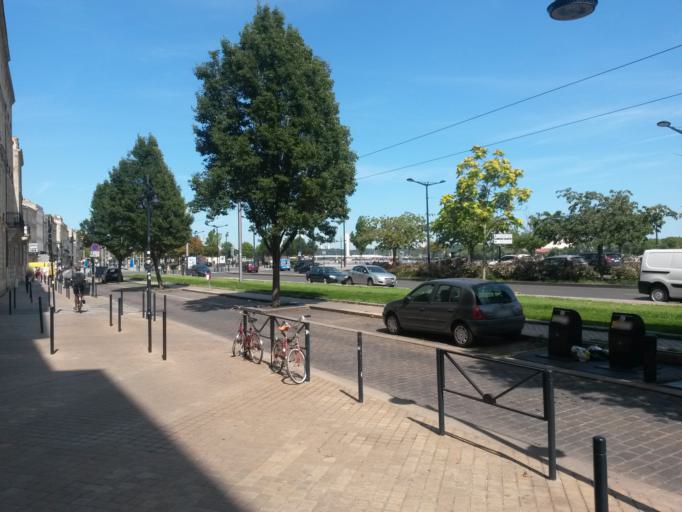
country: FR
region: Aquitaine
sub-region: Departement de la Gironde
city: Bordeaux
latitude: 44.8517
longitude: -0.5689
